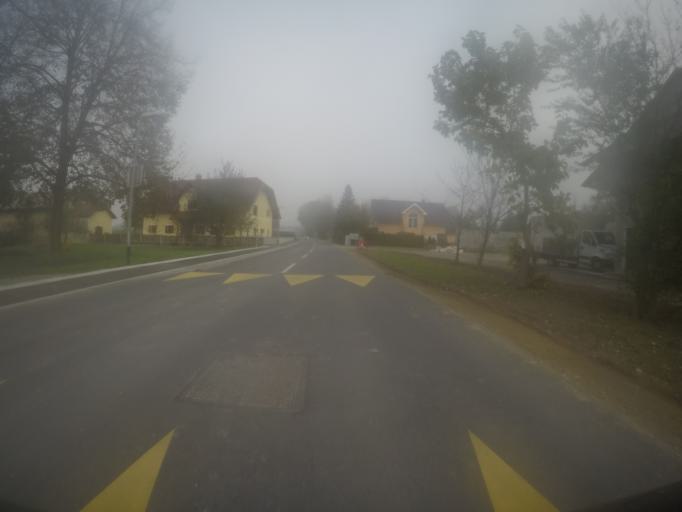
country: SI
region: Domzale
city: Dob
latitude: 46.1601
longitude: 14.6282
